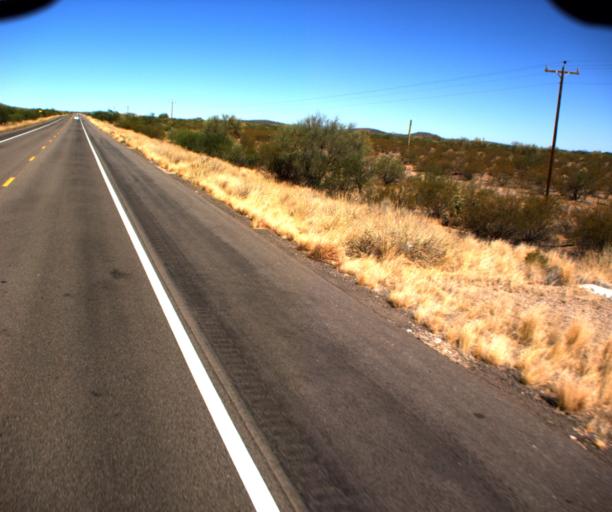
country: US
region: Arizona
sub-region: Pima County
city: Three Points
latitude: 32.0402
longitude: -111.4764
